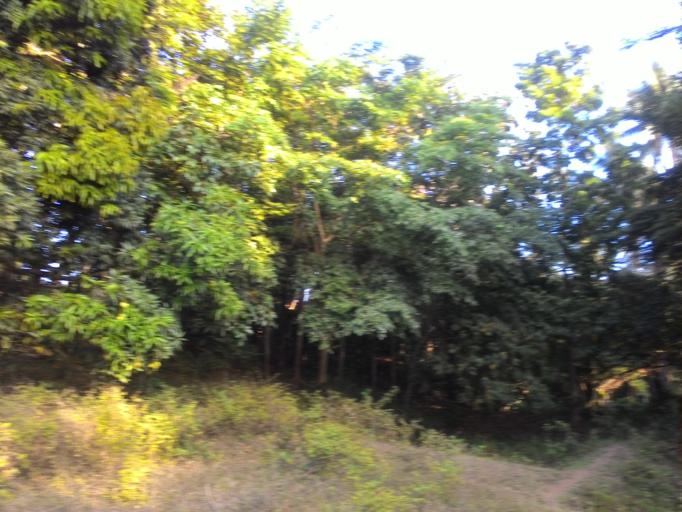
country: PH
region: Calabarzon
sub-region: Province of Cavite
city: Silang
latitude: 14.2324
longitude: 120.9403
